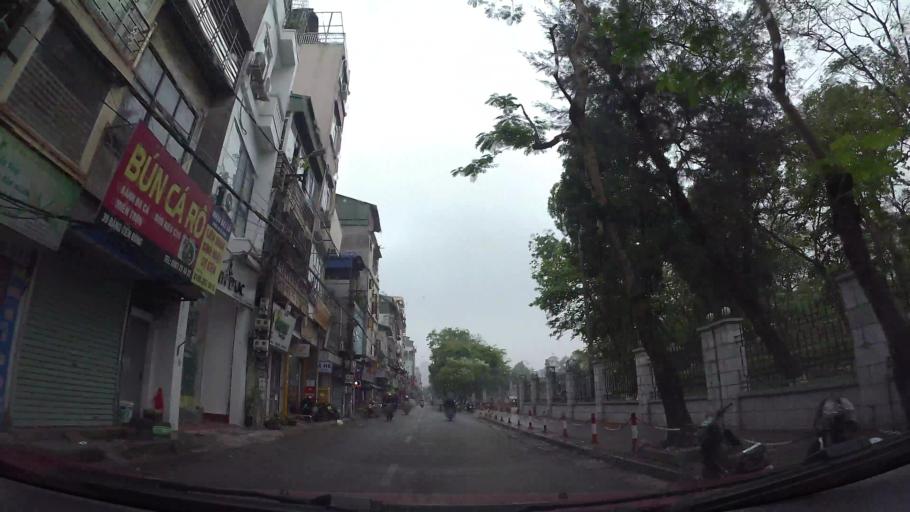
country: VN
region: Ha Noi
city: Dong Da
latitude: 21.0112
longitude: 105.8246
